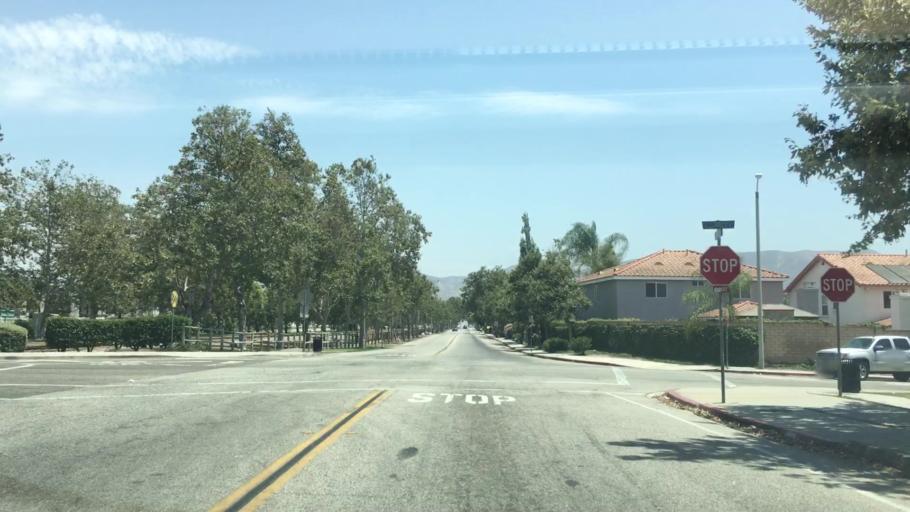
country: US
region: California
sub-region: Ventura County
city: Fillmore
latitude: 34.4046
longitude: -118.9291
